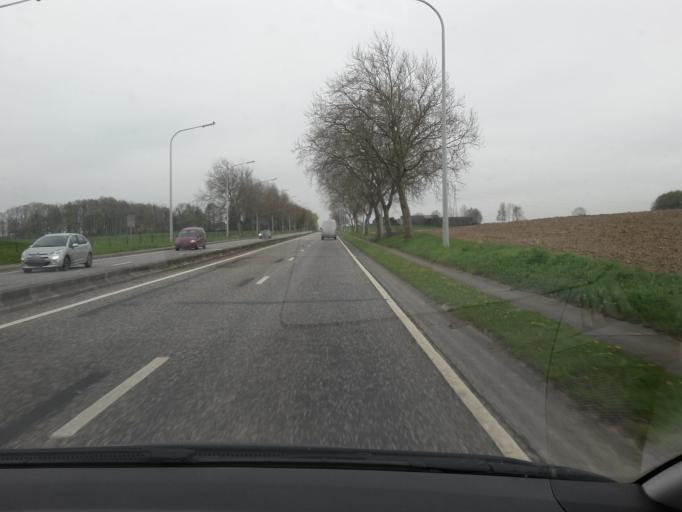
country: BE
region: Wallonia
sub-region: Province du Brabant Wallon
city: Genappe
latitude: 50.6381
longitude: 4.4249
